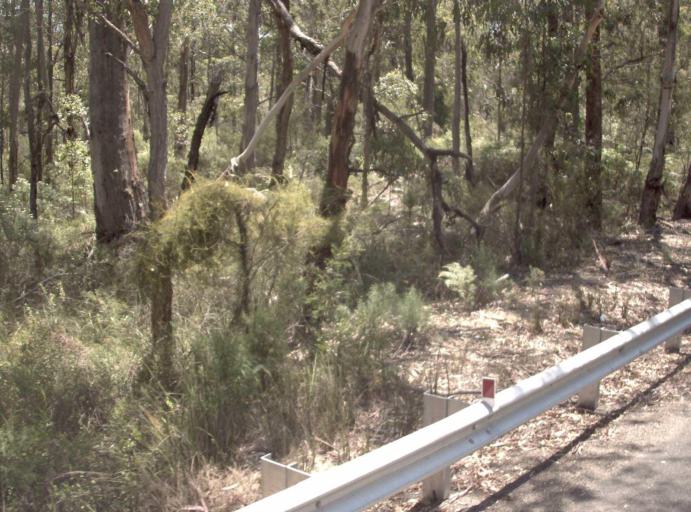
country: AU
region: Victoria
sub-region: East Gippsland
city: Lakes Entrance
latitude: -37.8274
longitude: 148.0336
